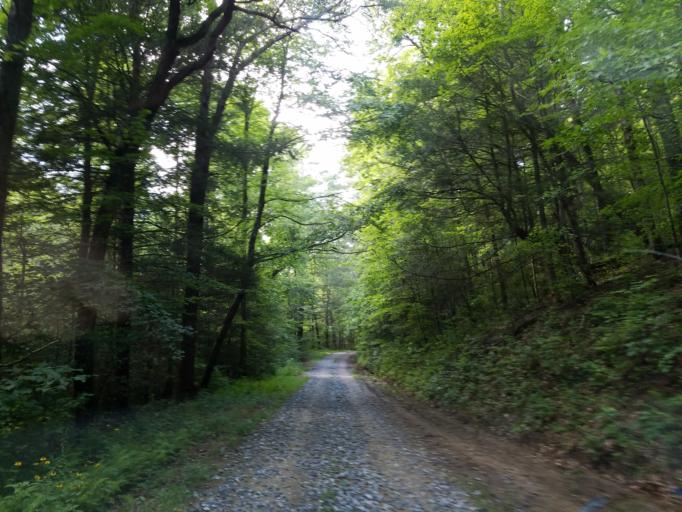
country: US
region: Georgia
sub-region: Lumpkin County
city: Dahlonega
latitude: 34.6786
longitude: -84.0424
